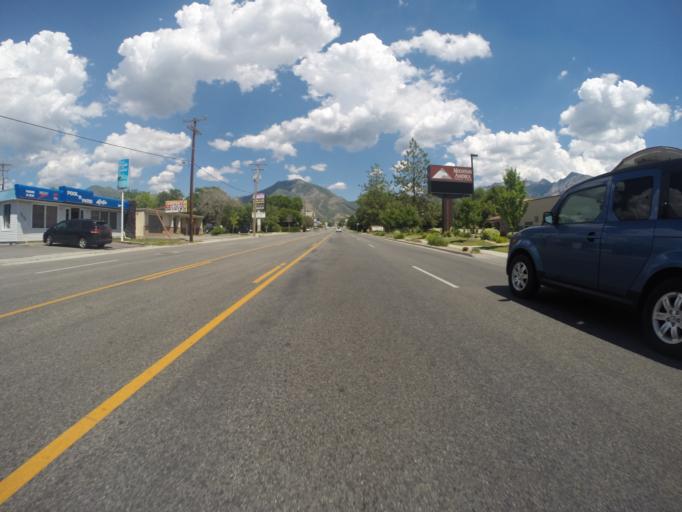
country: US
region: Utah
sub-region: Salt Lake County
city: Canyon Rim
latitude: 40.6999
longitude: -111.8285
